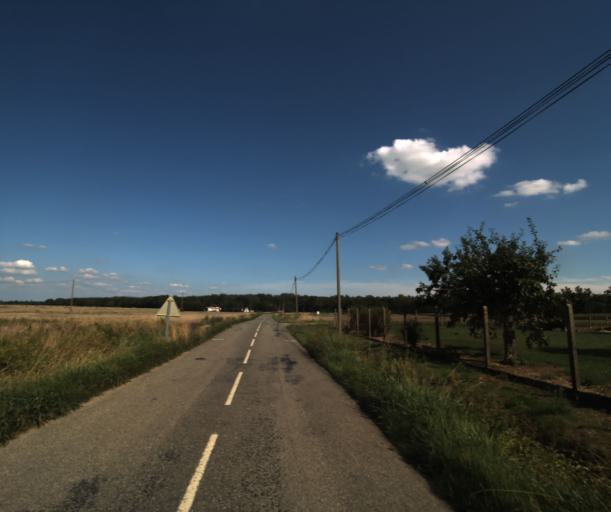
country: FR
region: Midi-Pyrenees
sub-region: Departement de la Haute-Garonne
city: Fonsorbes
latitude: 43.4992
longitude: 1.2210
